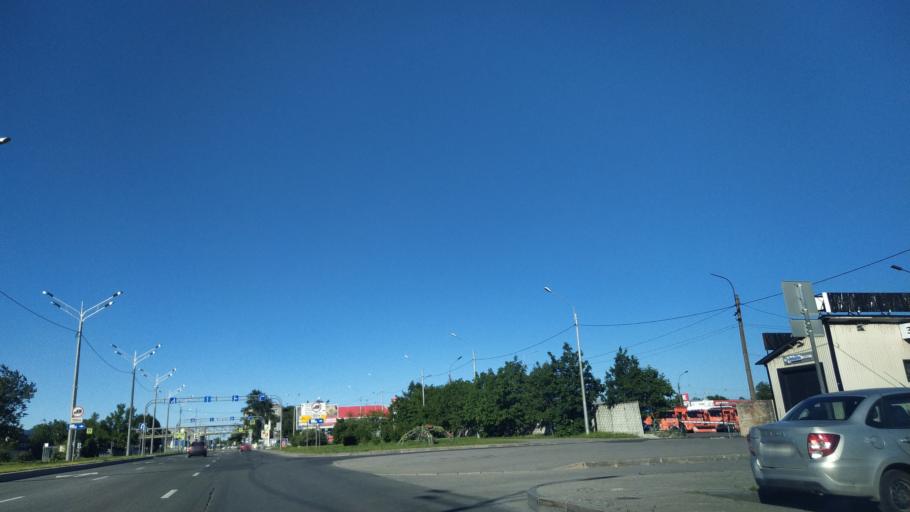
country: RU
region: St.-Petersburg
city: Kupchino
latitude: 59.8881
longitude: 30.3779
